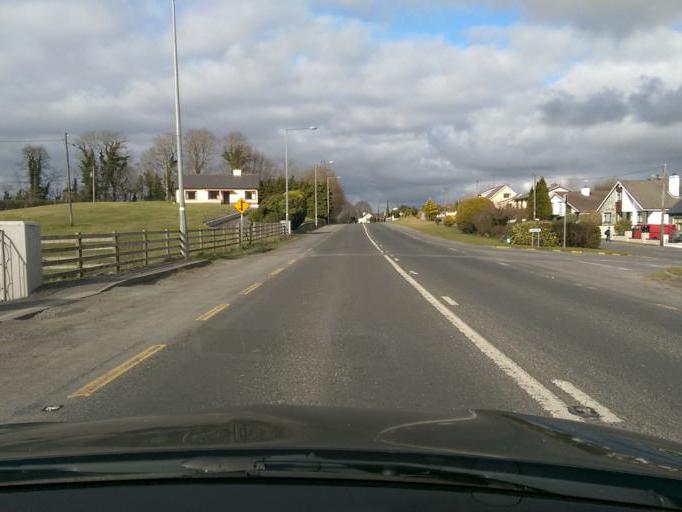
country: IE
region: Leinster
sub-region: An Iarmhi
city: Athlone
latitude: 53.4062
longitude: -7.9856
